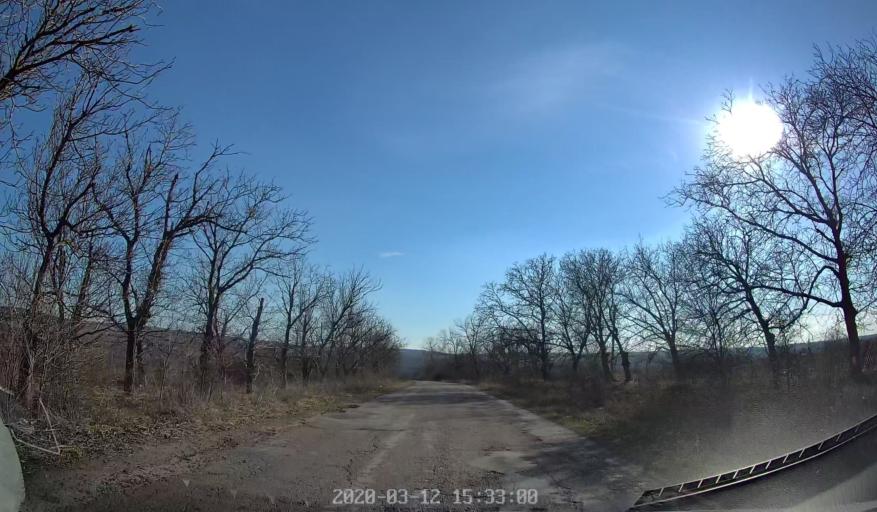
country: MD
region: Chisinau
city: Ciorescu
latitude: 47.1470
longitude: 28.9387
